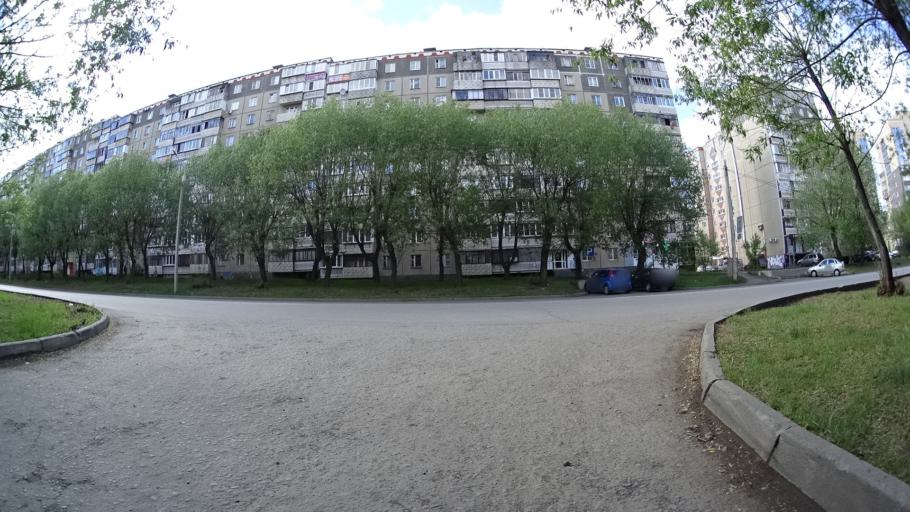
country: RU
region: Chelyabinsk
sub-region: Gorod Chelyabinsk
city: Chelyabinsk
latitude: 55.1765
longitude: 61.2965
